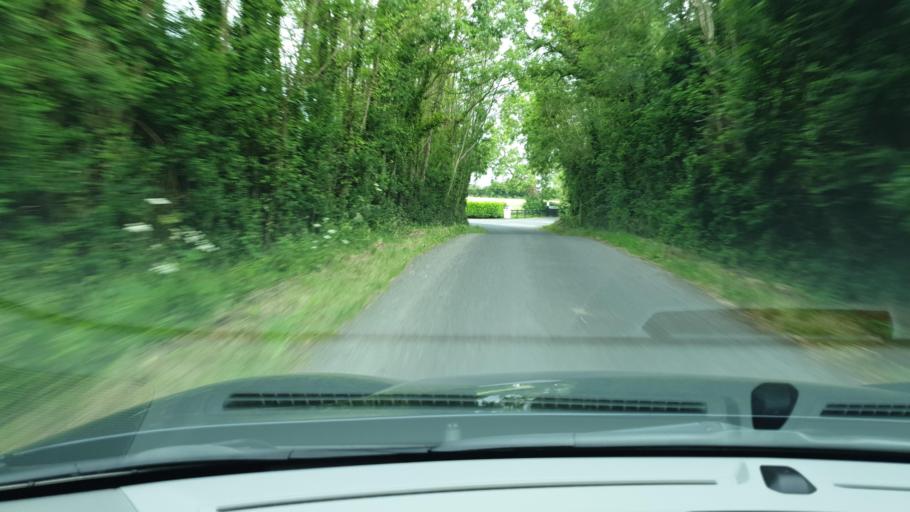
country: IE
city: Confey
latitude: 53.3991
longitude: -6.5068
